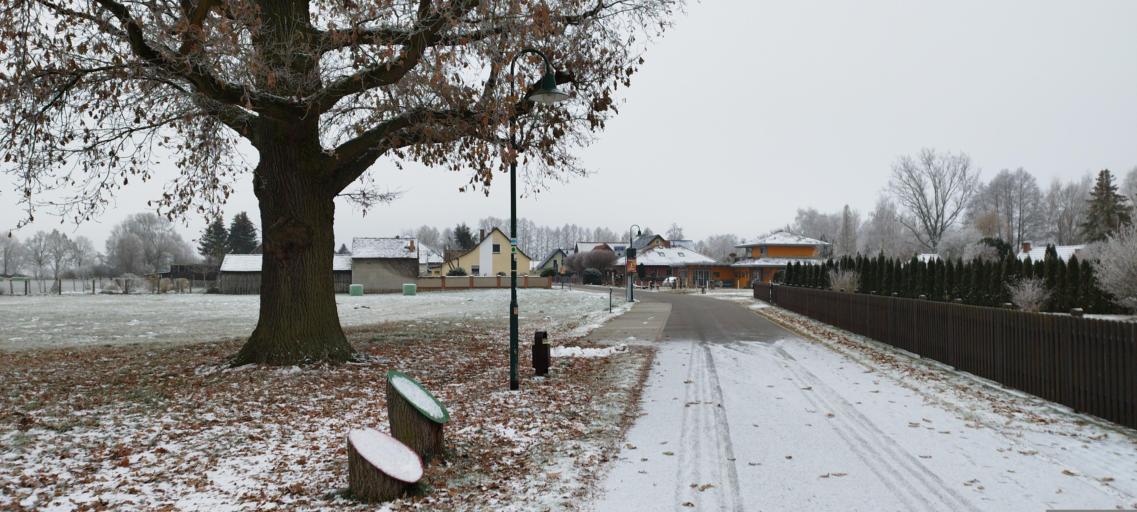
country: DE
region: Brandenburg
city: Schlepzig
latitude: 52.0260
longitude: 13.8891
